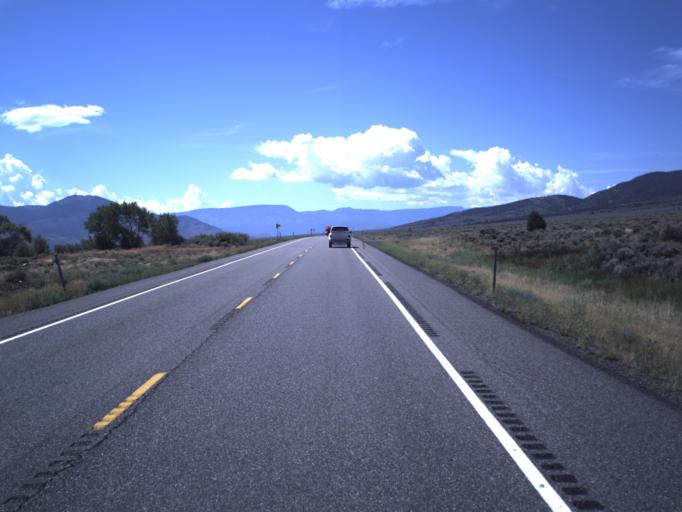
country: US
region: Utah
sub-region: Piute County
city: Junction
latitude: 38.3848
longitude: -112.2292
